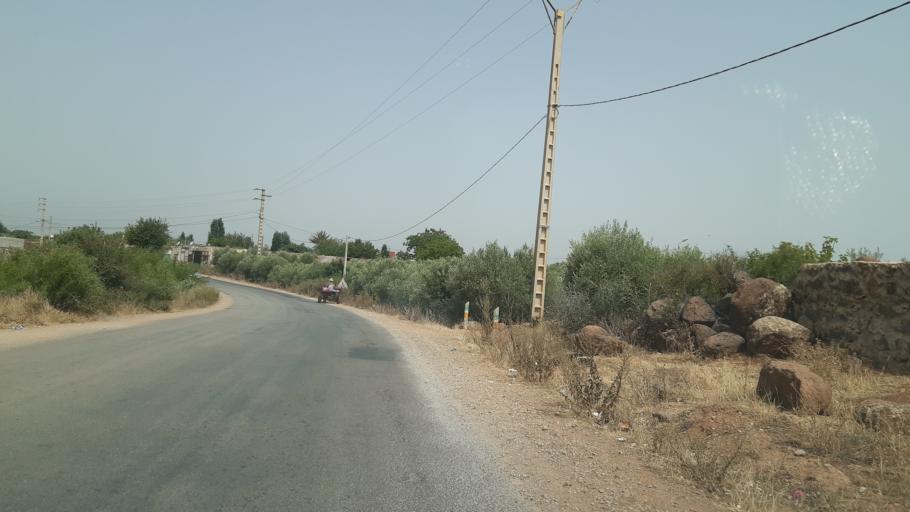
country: MA
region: Fes-Boulemane
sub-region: Fes
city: Oulad Tayeb
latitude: 33.8403
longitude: -5.1231
